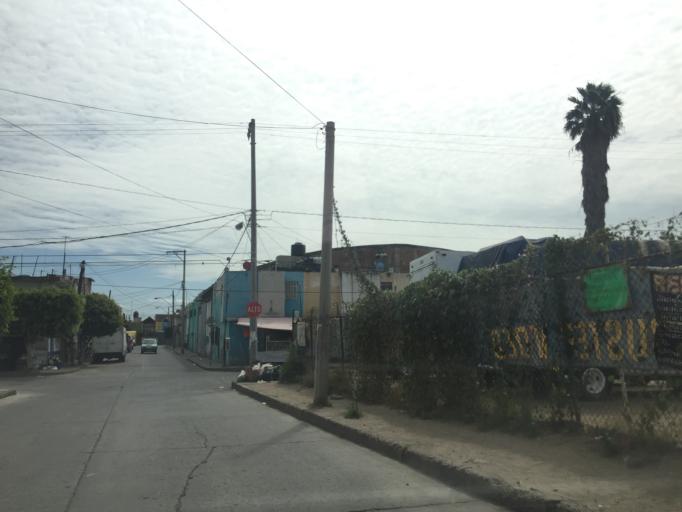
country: MX
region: Guanajuato
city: Leon
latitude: 21.1030
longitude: -101.7023
